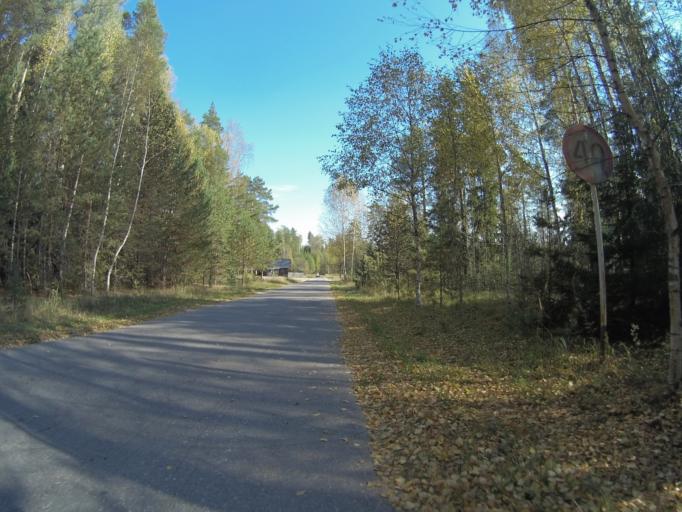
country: RU
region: Vladimir
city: Sobinka
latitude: 55.8624
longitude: 40.1521
